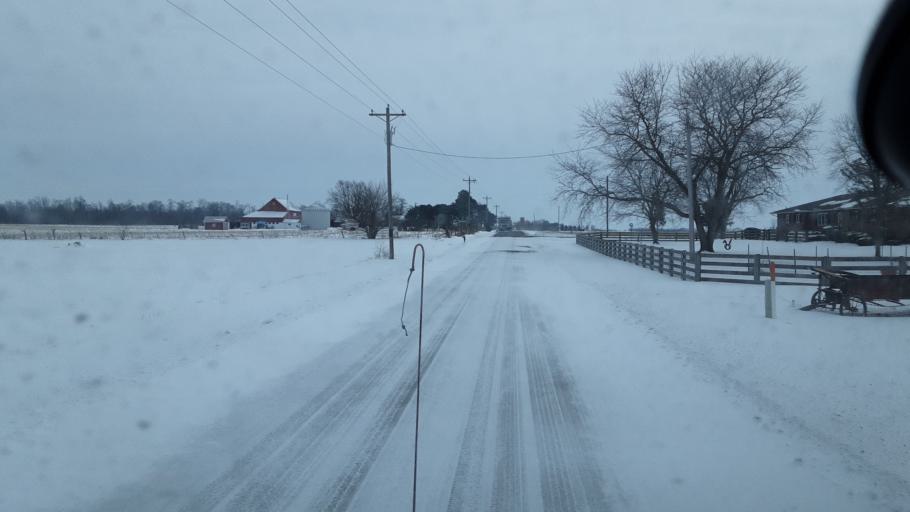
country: US
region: Ohio
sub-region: Union County
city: Marysville
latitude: 40.1676
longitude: -83.3677
